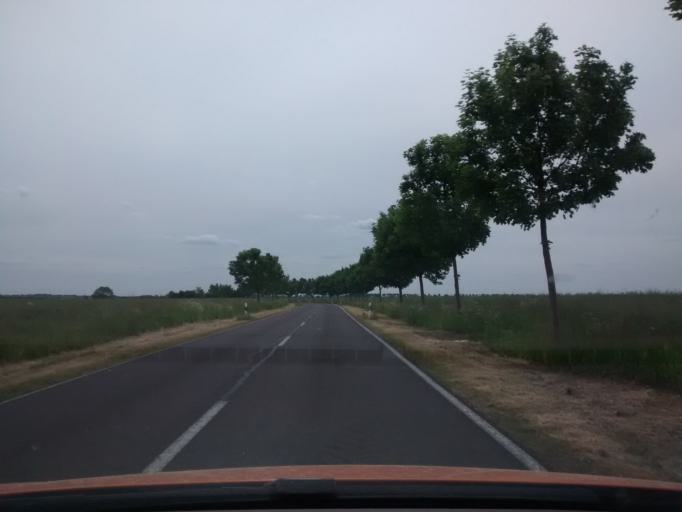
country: DE
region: Brandenburg
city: Juterbog
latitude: 51.9698
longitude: 13.0750
